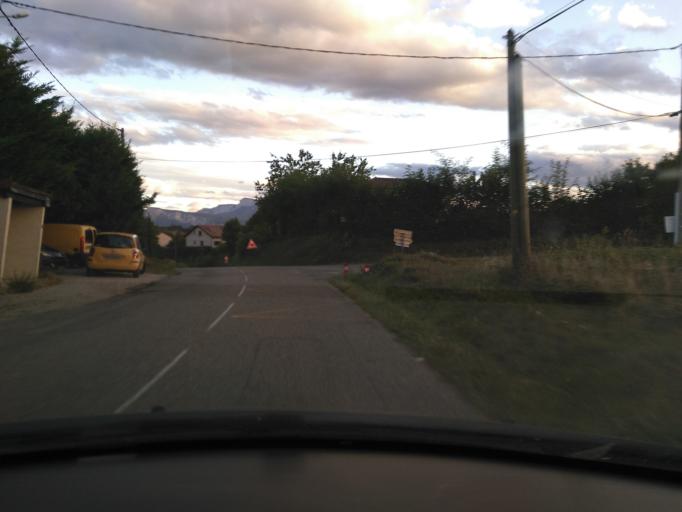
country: FR
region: Rhone-Alpes
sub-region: Departement de l'Isere
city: La Murette
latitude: 45.3728
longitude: 5.5245
